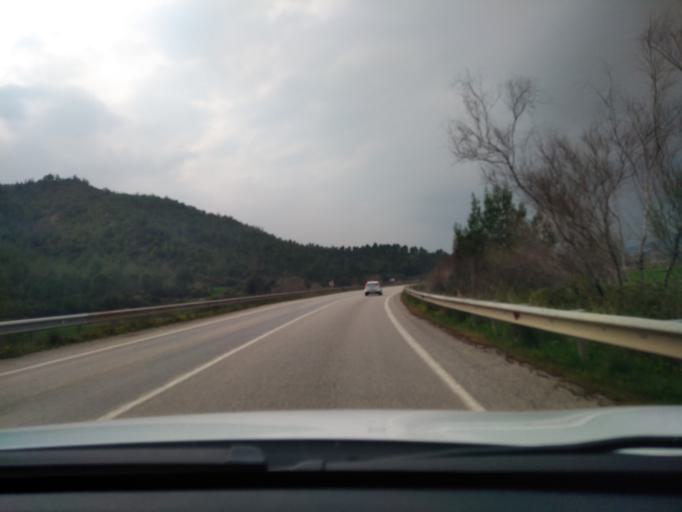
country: TR
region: Mersin
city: Yenice
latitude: 37.0915
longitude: 35.1395
